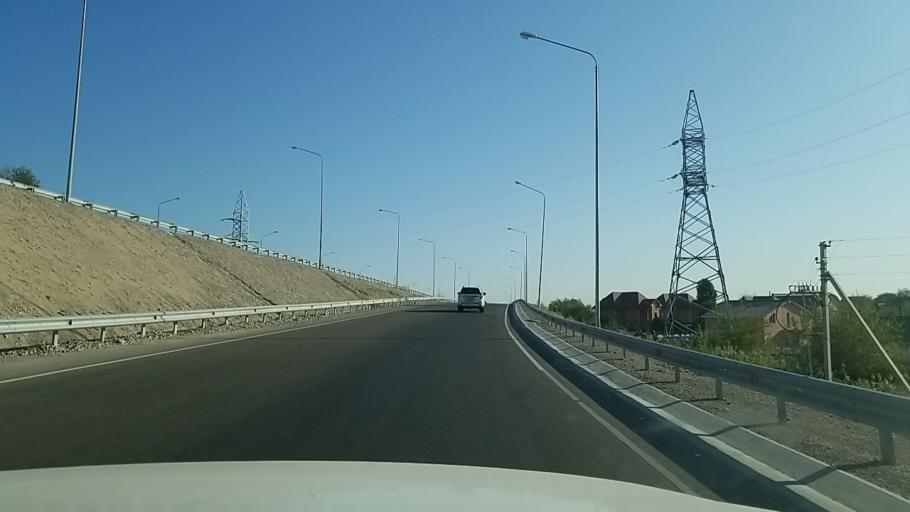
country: KZ
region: Almaty Oblysy
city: Energeticheskiy
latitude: 43.4404
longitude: 76.9894
